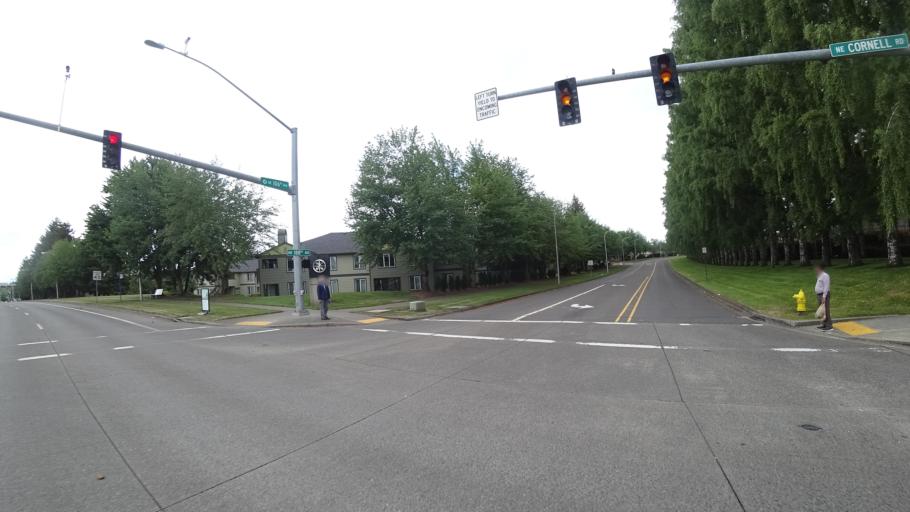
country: US
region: Oregon
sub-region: Washington County
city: Rockcreek
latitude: 45.5344
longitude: -122.8710
